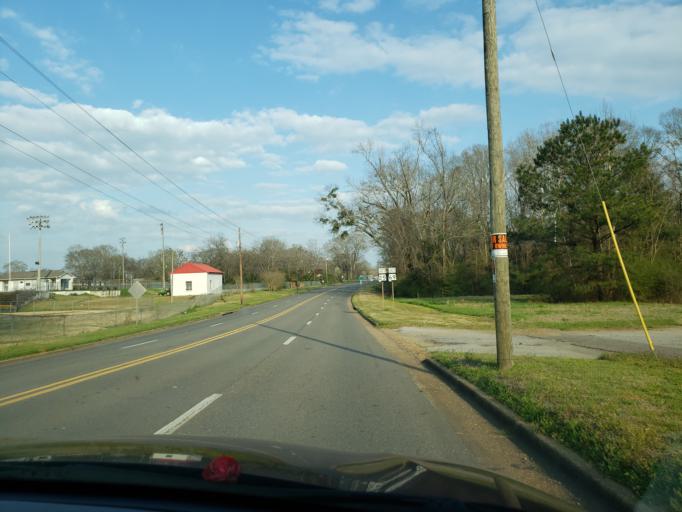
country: US
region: Alabama
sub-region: Hale County
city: Greensboro
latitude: 32.7007
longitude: -87.6033
